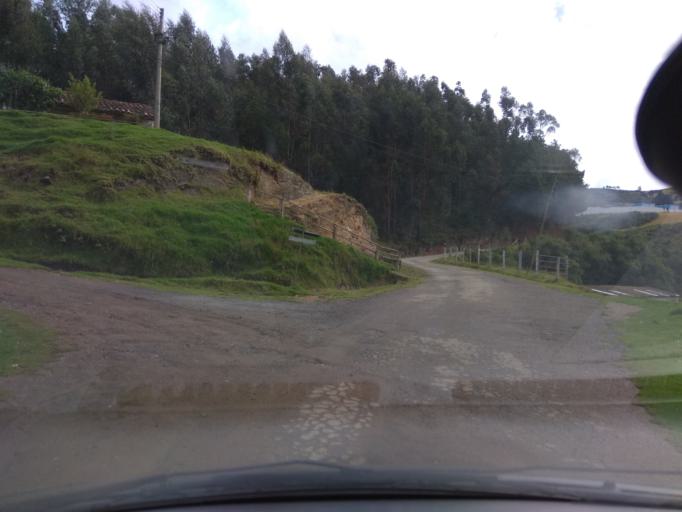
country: CO
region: Boyaca
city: Santa Rosa de Viterbo
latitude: 5.8902
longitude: -72.9748
